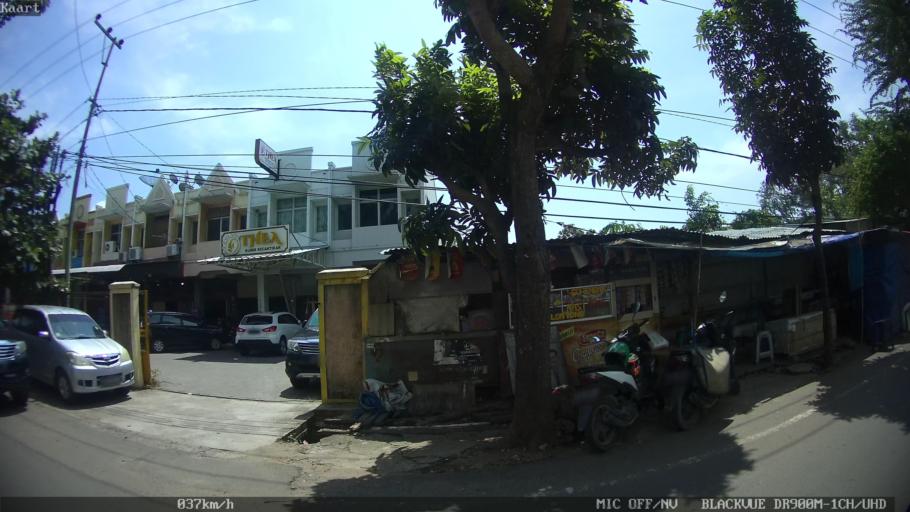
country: ID
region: Lampung
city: Kedaton
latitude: -5.3841
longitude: 105.2815
